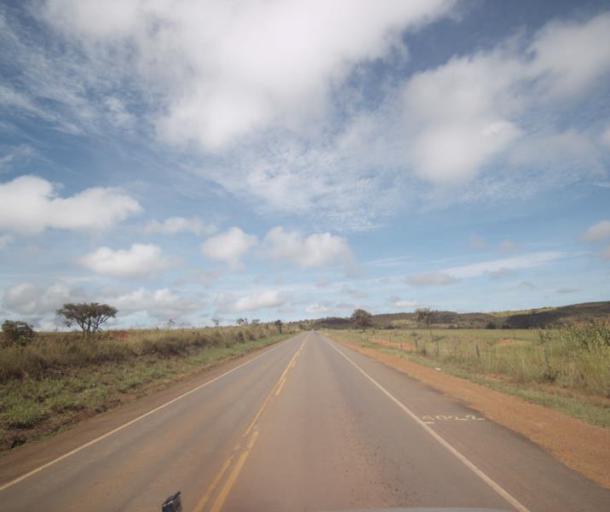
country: BR
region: Goias
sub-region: Pirenopolis
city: Pirenopolis
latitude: -15.9998
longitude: -48.8398
